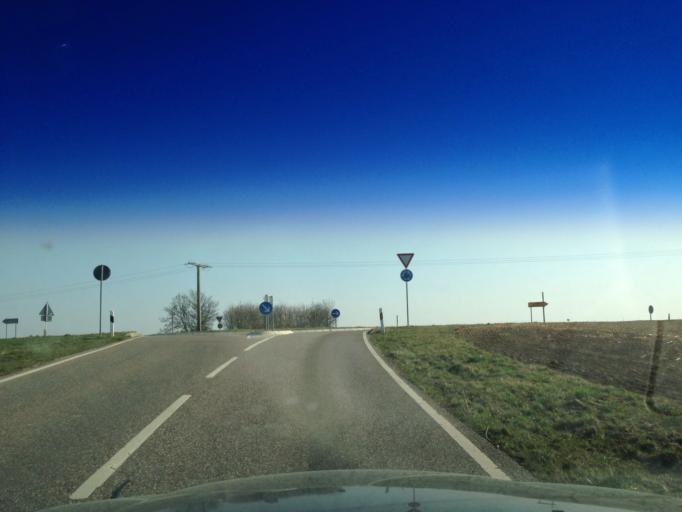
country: DE
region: Baden-Wuerttemberg
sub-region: Regierungsbezirk Stuttgart
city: Vaihingen an der Enz
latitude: 48.9226
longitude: 8.9310
